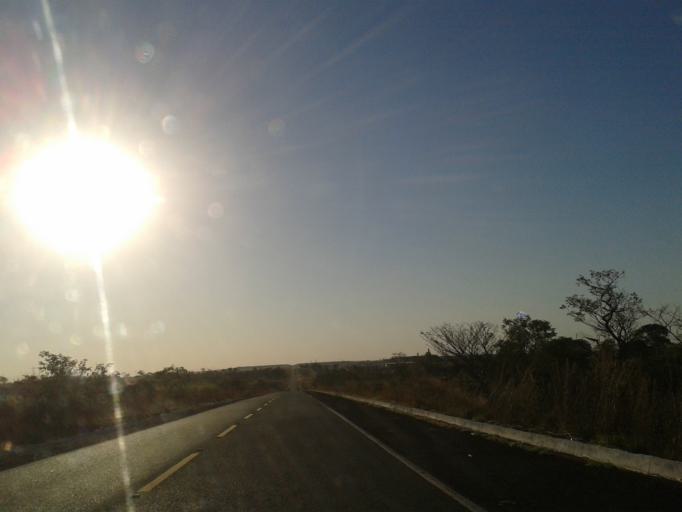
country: BR
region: Minas Gerais
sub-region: Santa Vitoria
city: Santa Vitoria
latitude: -19.0826
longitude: -50.3565
